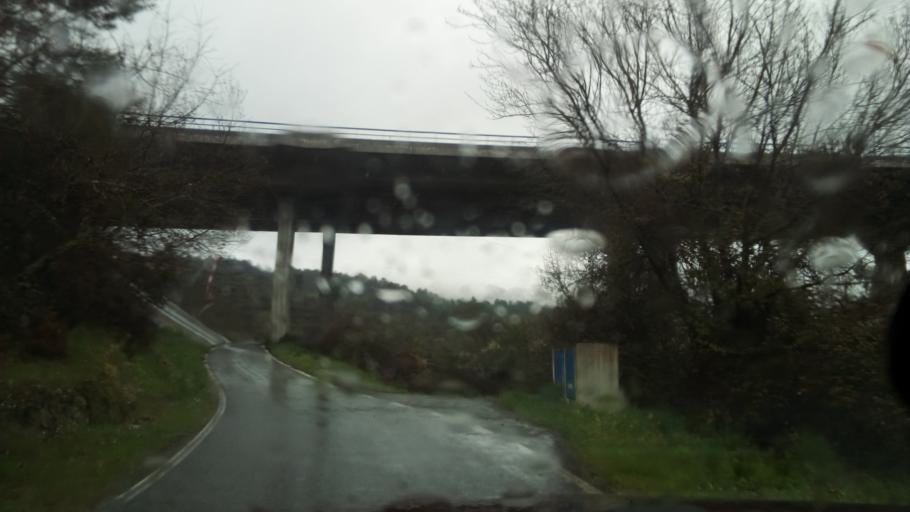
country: PT
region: Guarda
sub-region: Fornos de Algodres
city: Fornos de Algodres
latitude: 40.6186
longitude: -7.5175
